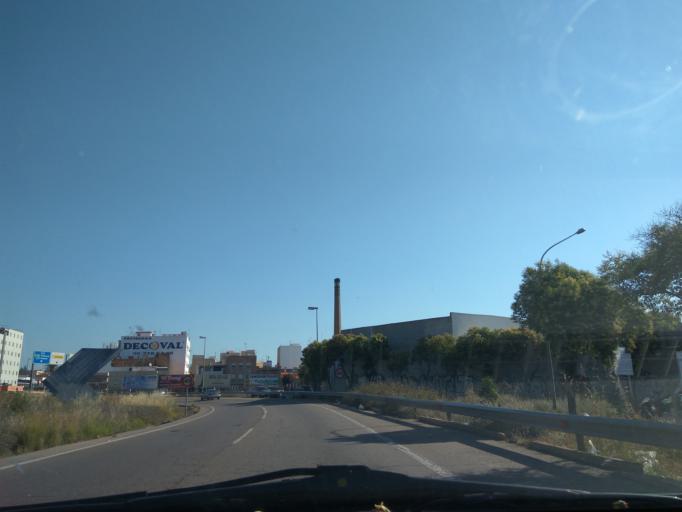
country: ES
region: Valencia
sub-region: Provincia de Valencia
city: Manises
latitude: 39.4920
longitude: -0.4693
